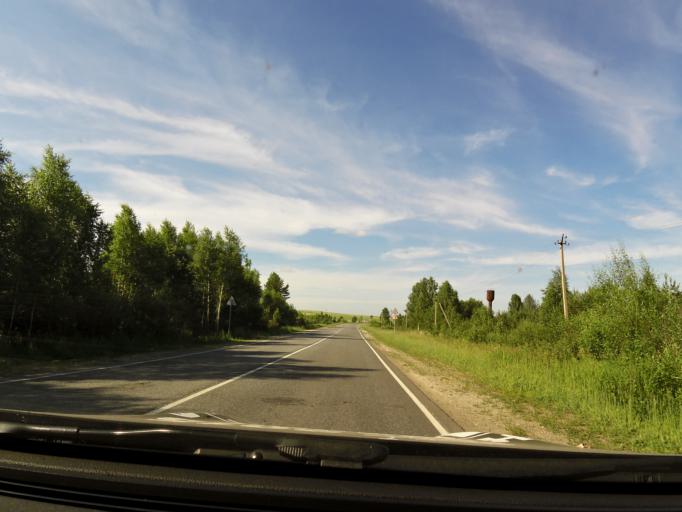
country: RU
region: Kirov
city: Belaya Kholunitsa
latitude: 58.8878
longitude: 50.8747
